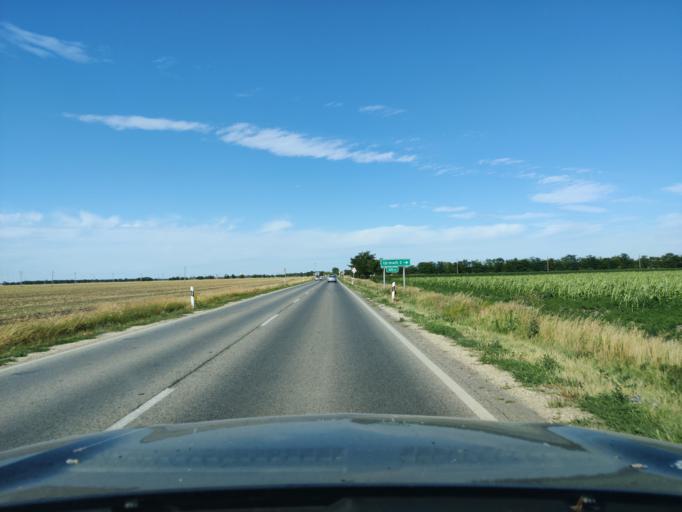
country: HU
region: Gyor-Moson-Sopron
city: Janossomorja
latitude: 47.8192
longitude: 17.1913
